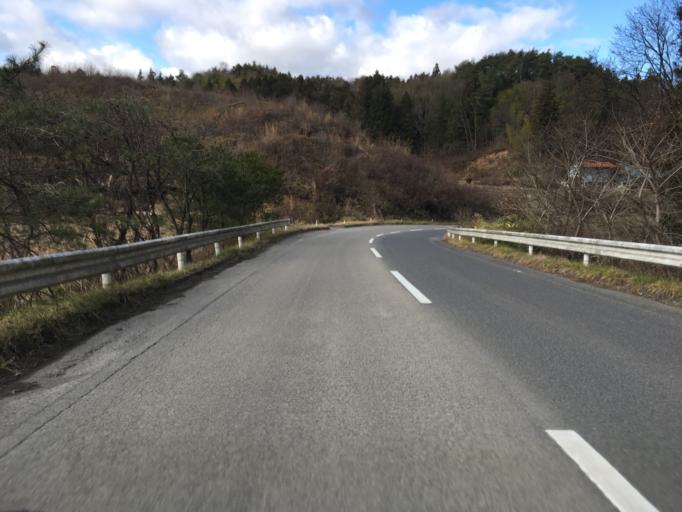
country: JP
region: Fukushima
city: Ishikawa
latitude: 37.2171
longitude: 140.5498
